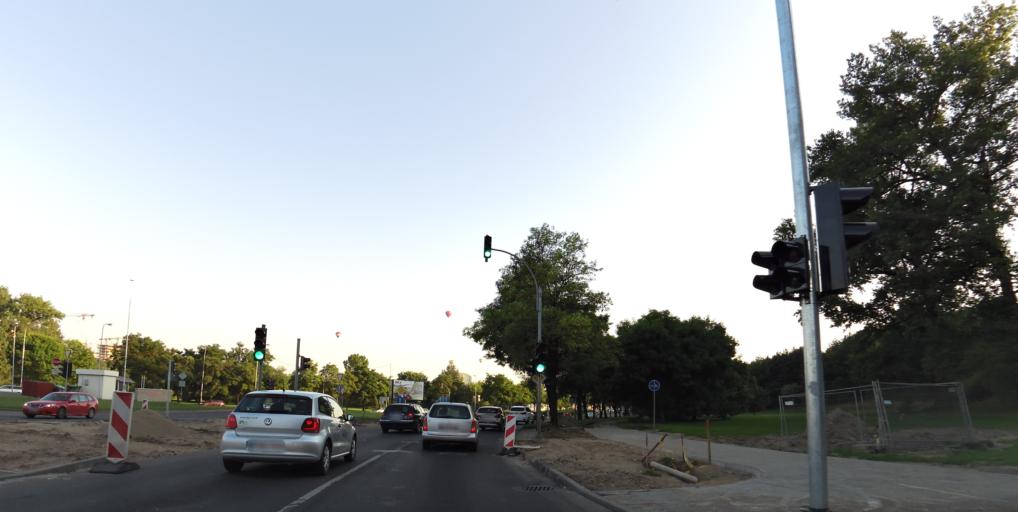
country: LT
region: Vilnius County
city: Seskine
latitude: 54.7046
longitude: 25.2661
